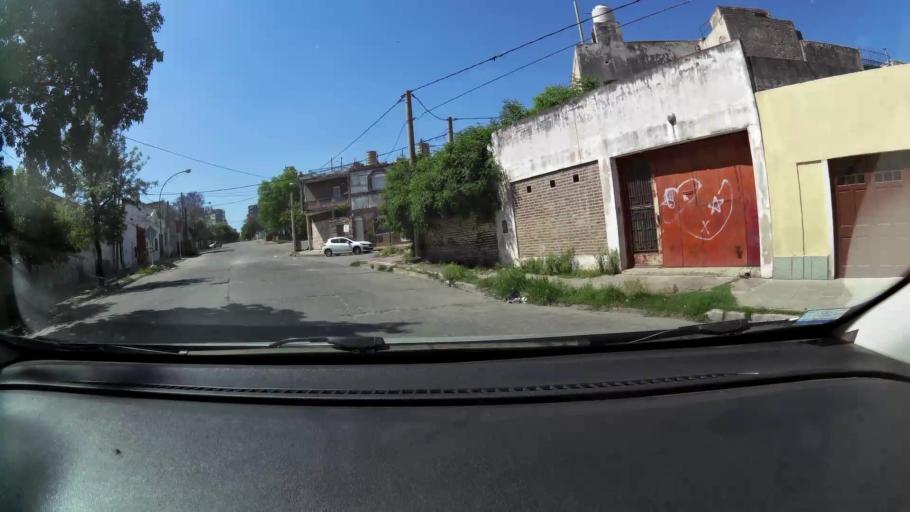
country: AR
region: Cordoba
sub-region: Departamento de Capital
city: Cordoba
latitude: -31.4046
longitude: -64.1773
